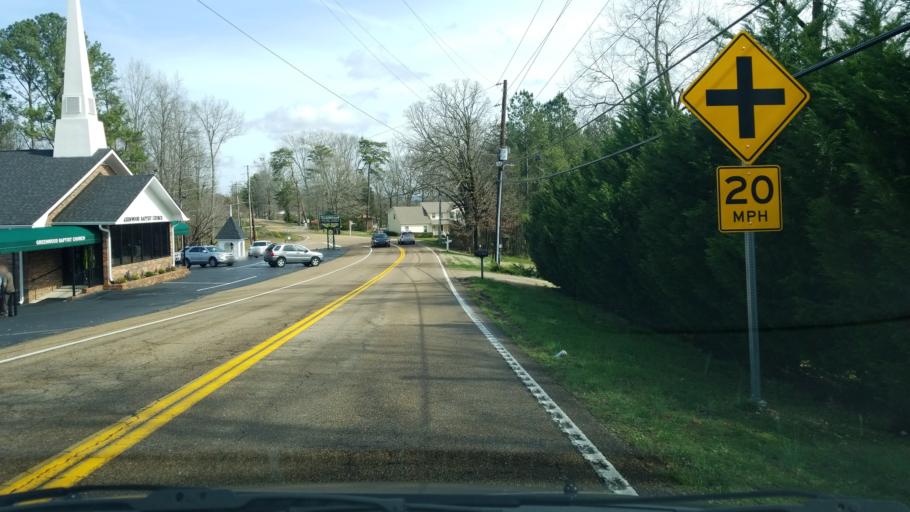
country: US
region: Tennessee
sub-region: Hamilton County
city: Lakesite
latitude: 35.1660
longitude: -85.0587
